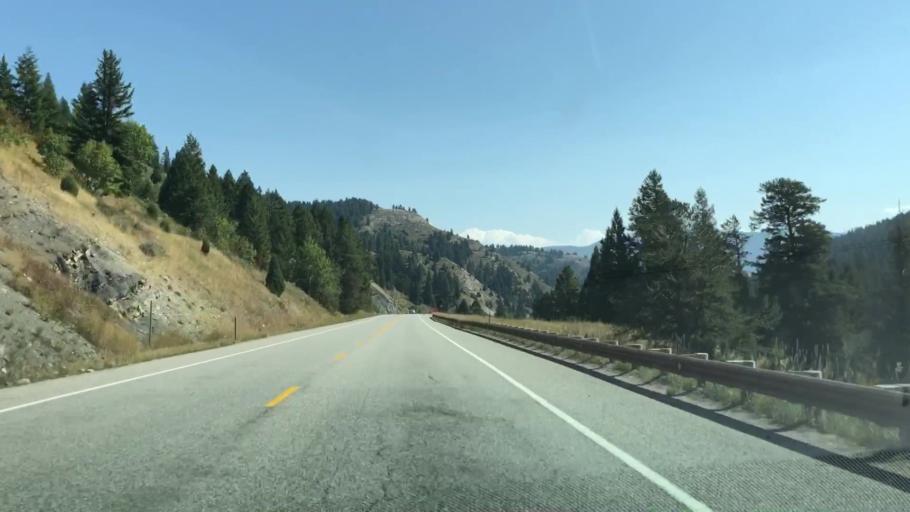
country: US
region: Wyoming
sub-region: Teton County
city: Hoback
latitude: 43.2008
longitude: -110.8664
